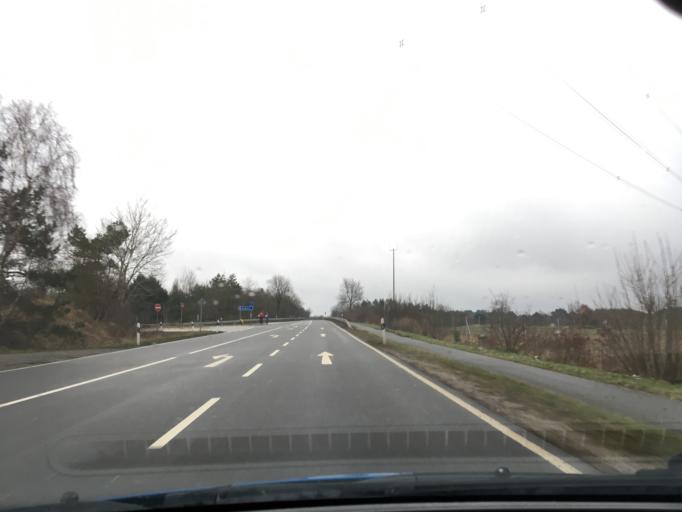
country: DE
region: Schleswig-Holstein
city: Hornbek
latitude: 53.5500
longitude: 10.6425
